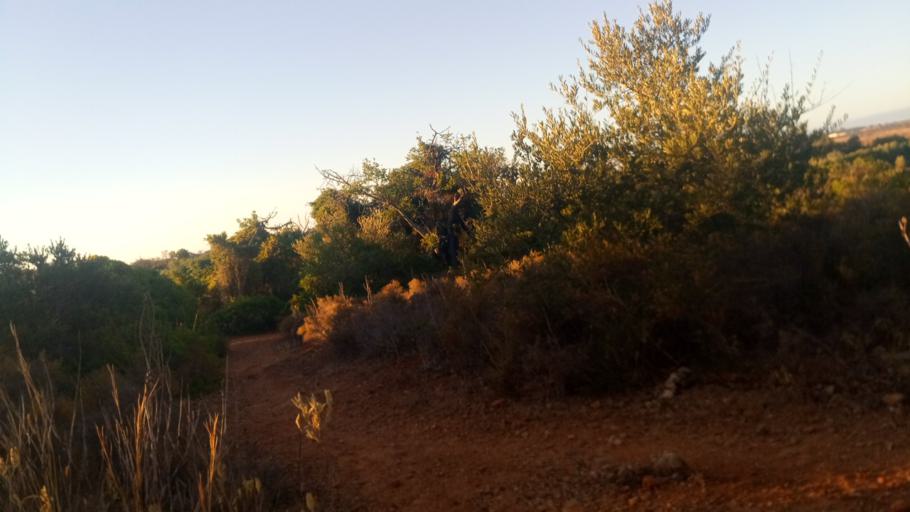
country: PT
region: Faro
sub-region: Tavira
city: Tavira
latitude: 37.1408
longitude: -7.6127
